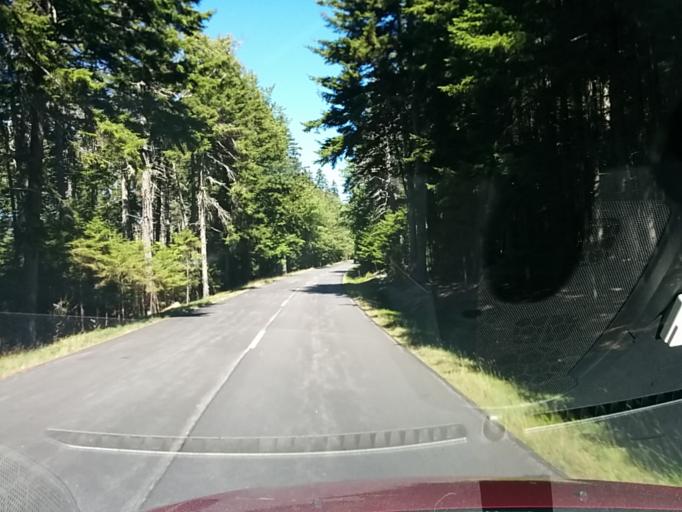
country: US
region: Maine
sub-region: Hancock County
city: Bar Harbor
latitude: 44.3008
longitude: -68.2175
